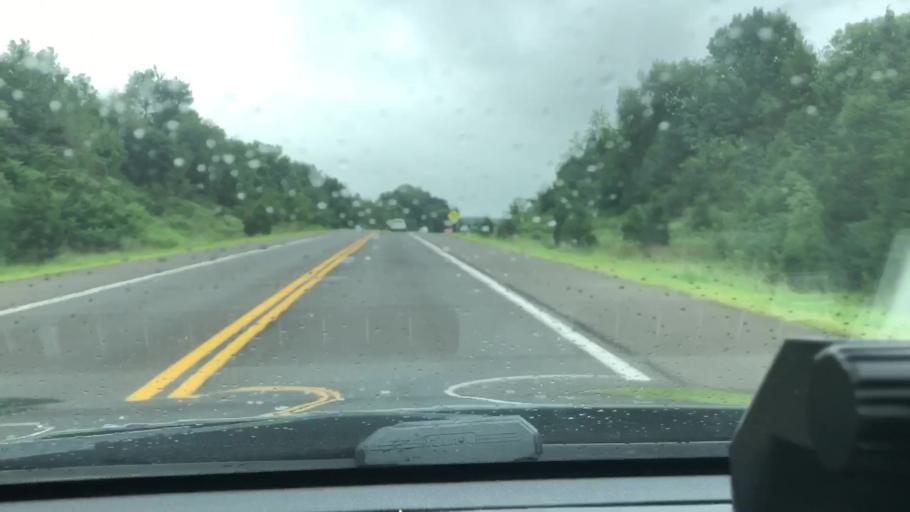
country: US
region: Pennsylvania
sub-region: Bucks County
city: Spinnerstown
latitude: 40.4312
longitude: -75.4335
